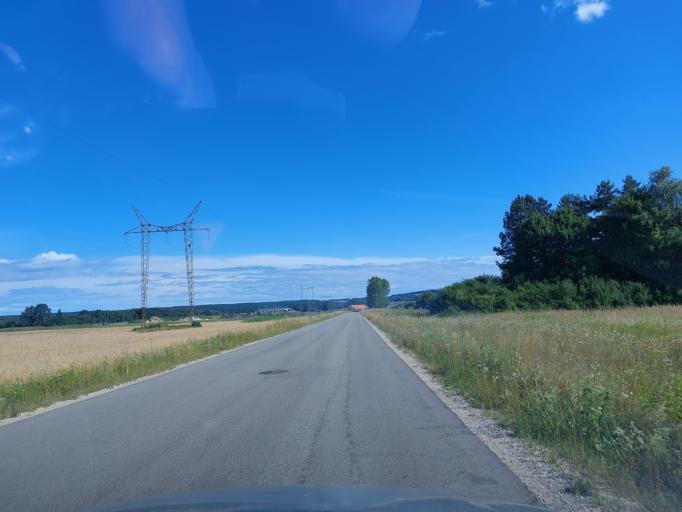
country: HU
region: Veszprem
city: Ajka
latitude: 47.1229
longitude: 17.5388
